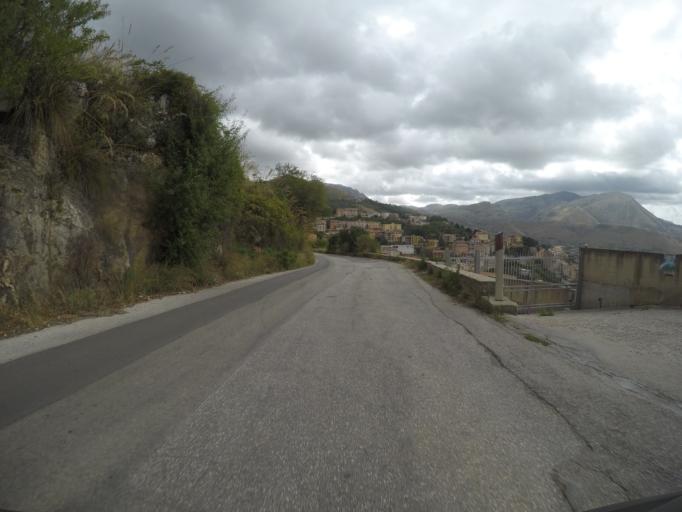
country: IT
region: Sicily
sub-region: Palermo
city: Montelepre
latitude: 38.0933
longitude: 13.1743
